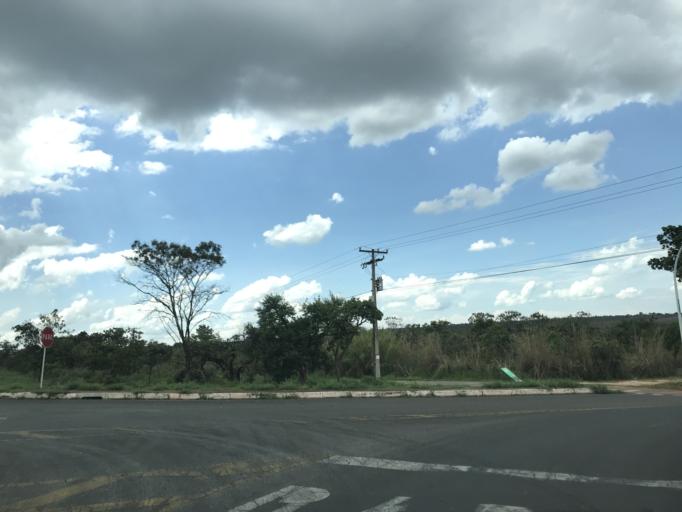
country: BR
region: Federal District
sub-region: Brasilia
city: Brasilia
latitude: -15.6835
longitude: -47.8652
